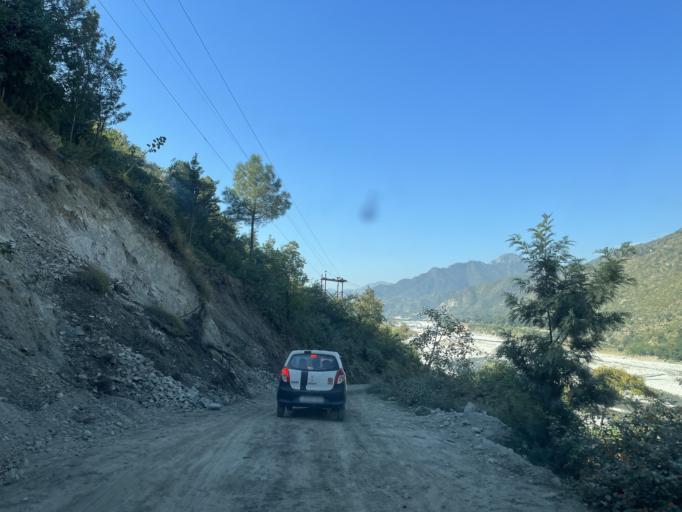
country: IN
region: Uttarakhand
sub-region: Almora
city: Ranikhet
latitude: 29.5536
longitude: 79.3962
